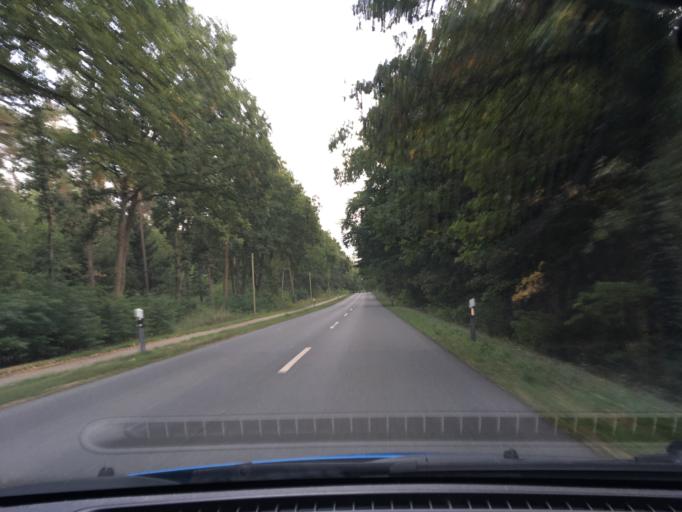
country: DE
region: Lower Saxony
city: Westergellersen
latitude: 53.2452
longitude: 10.2341
